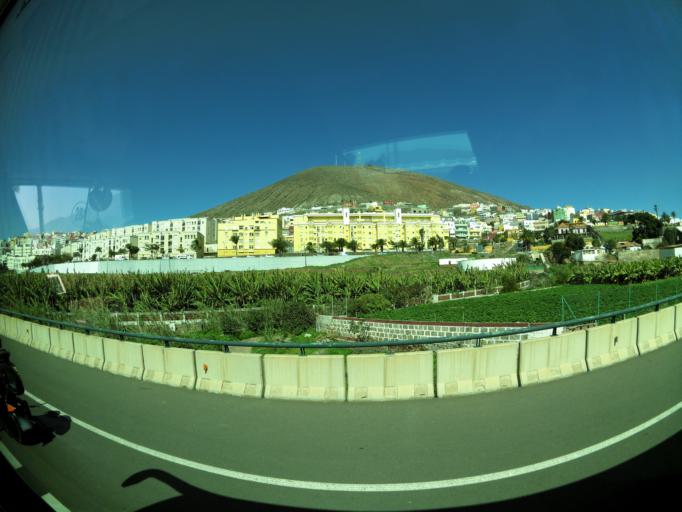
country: ES
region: Canary Islands
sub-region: Provincia de Las Palmas
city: Galdar
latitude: 28.1438
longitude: -15.6416
